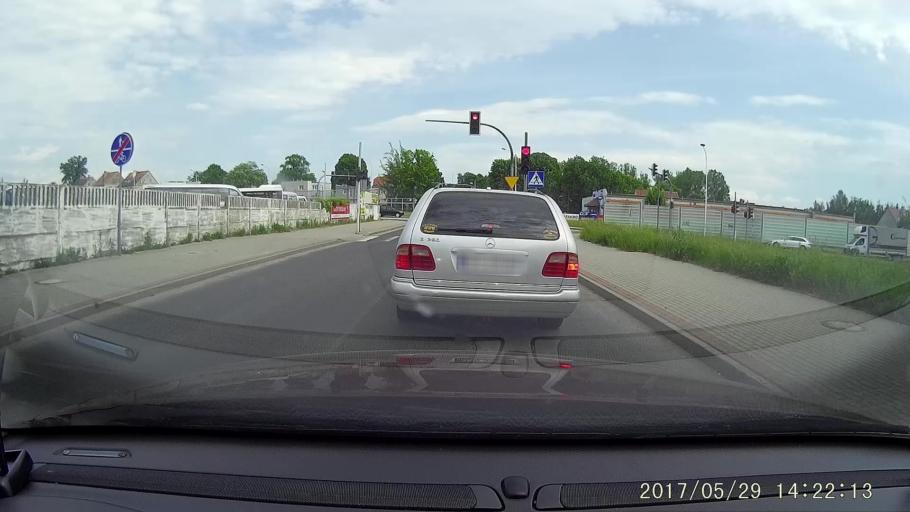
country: PL
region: Lower Silesian Voivodeship
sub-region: Powiat zgorzelecki
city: Zgorzelec
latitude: 51.1342
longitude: 15.0242
